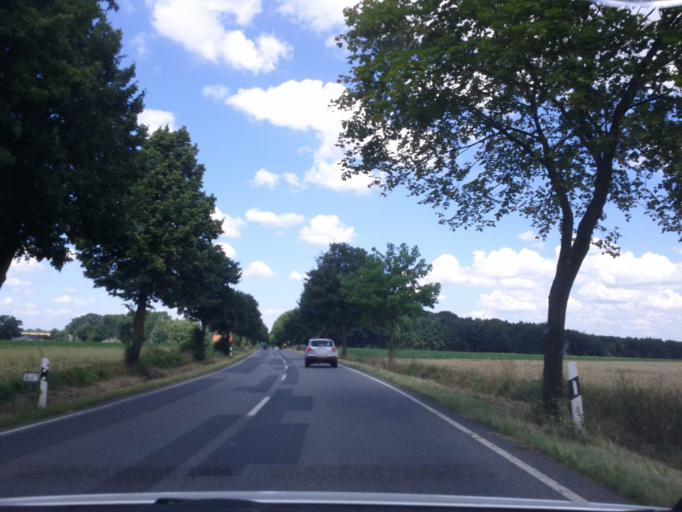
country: DE
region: Lower Saxony
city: Nottensdorf
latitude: 53.4650
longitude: 9.5975
